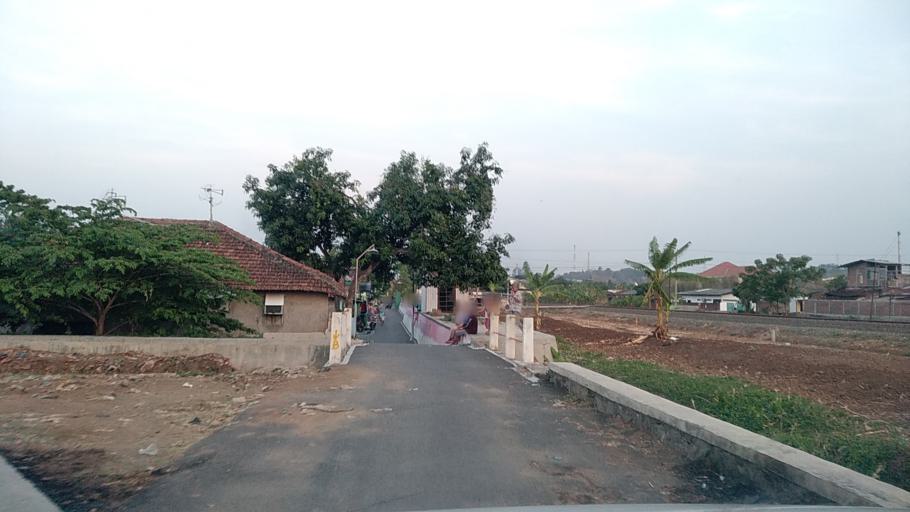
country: ID
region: Central Java
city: Semarang
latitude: -6.9731
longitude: 110.3181
